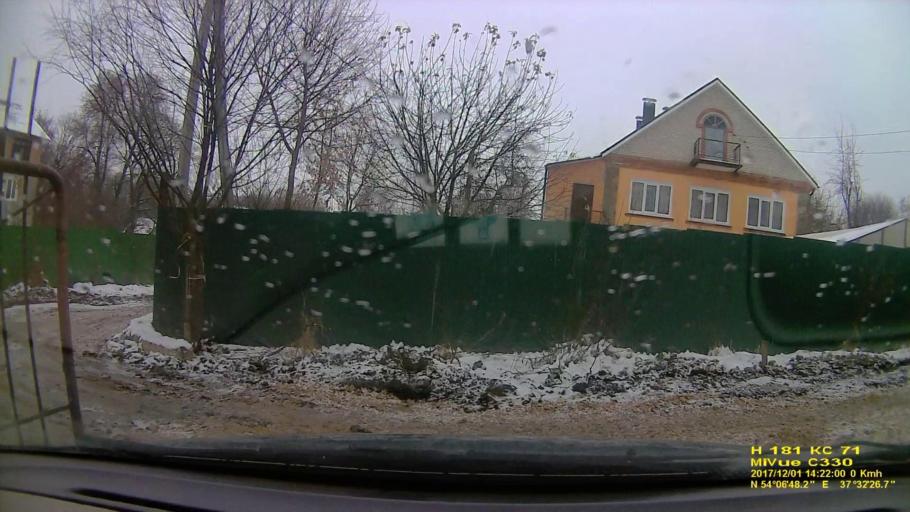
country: RU
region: Tula
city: Kosaya Gora
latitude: 54.1134
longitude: 37.5407
